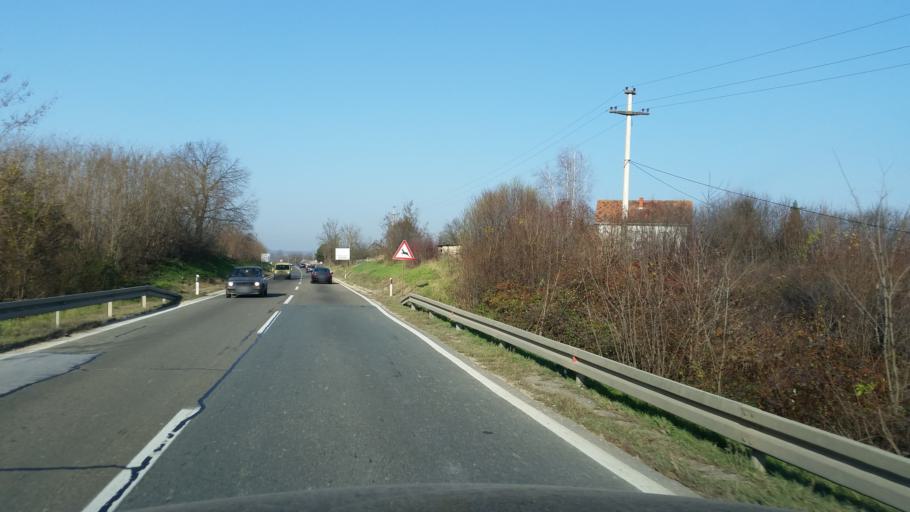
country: RS
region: Central Serbia
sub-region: Kolubarski Okrug
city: Ljig
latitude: 44.2674
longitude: 20.2849
